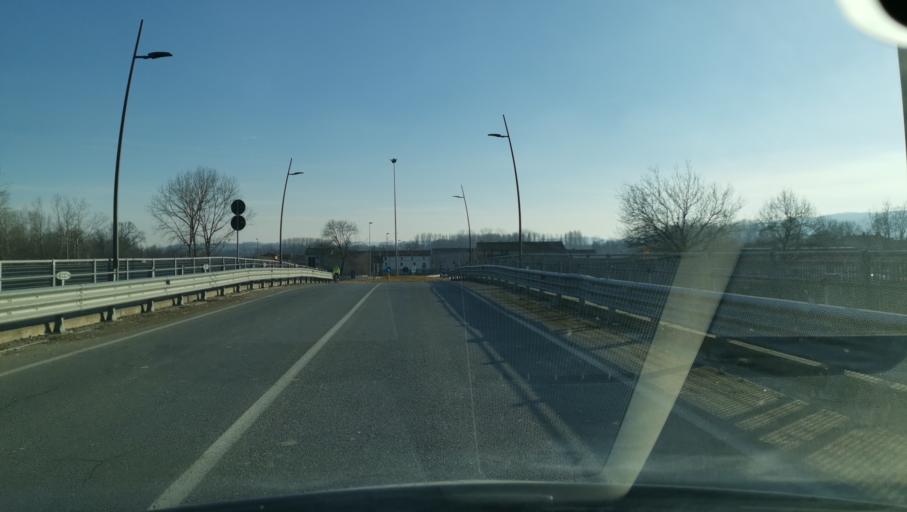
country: IT
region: Piedmont
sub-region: Provincia di Torino
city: Pavone Canavese
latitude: 45.4216
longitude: 7.8593
